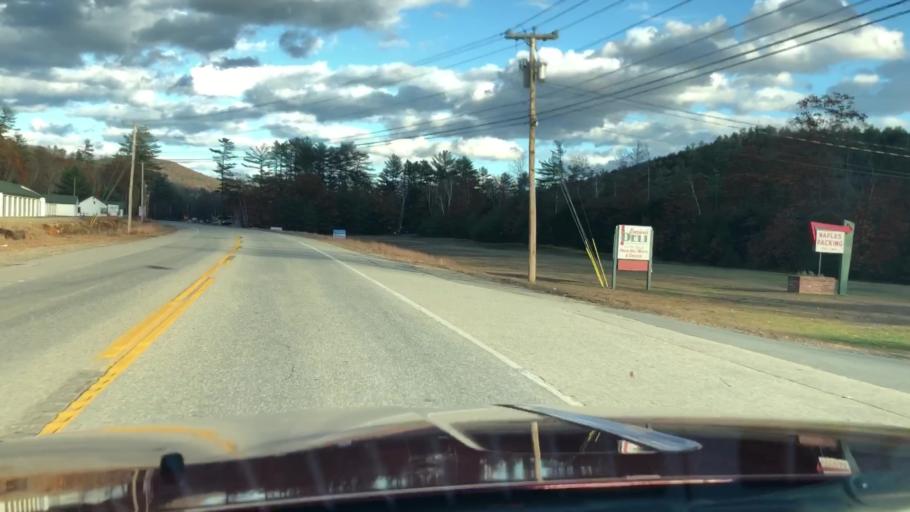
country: US
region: Maine
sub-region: Oxford County
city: Dixfield
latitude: 44.5313
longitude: -70.4821
